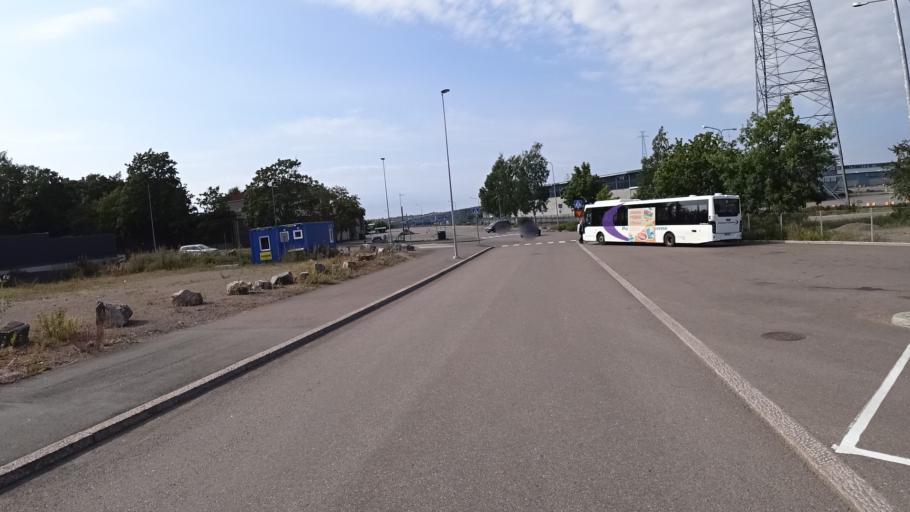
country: FI
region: Kymenlaakso
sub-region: Kotka-Hamina
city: Kotka
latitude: 60.4695
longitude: 26.9510
